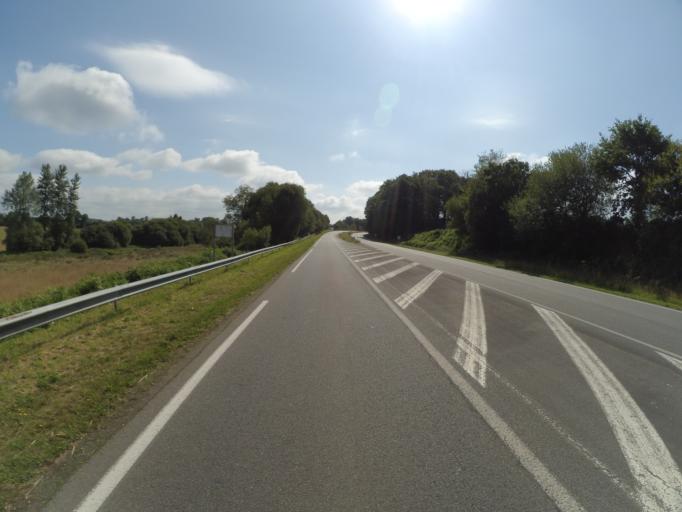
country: FR
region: Brittany
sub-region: Departement du Finistere
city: Bannalec
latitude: 47.9255
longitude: -3.6829
